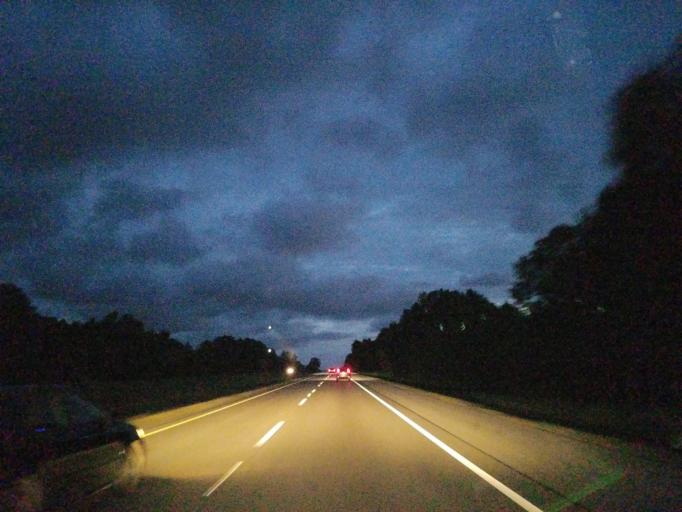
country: US
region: Mississippi
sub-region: Jones County
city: Sharon
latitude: 31.8273
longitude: -89.0512
